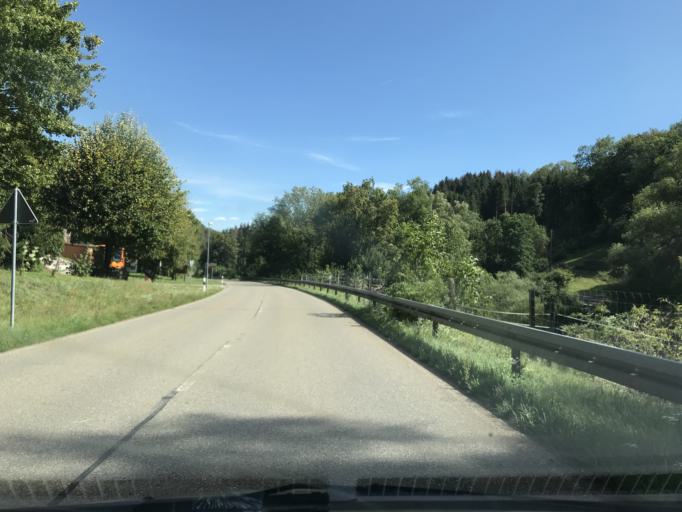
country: DE
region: Baden-Wuerttemberg
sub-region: Freiburg Region
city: Schworstadt
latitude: 47.6137
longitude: 7.8608
